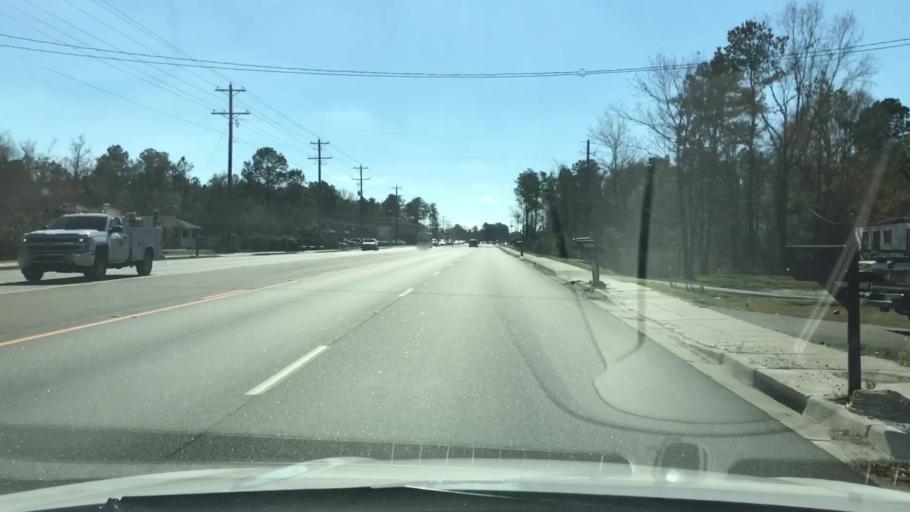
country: US
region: South Carolina
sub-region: Horry County
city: Garden City
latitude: 33.6361
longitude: -79.0333
